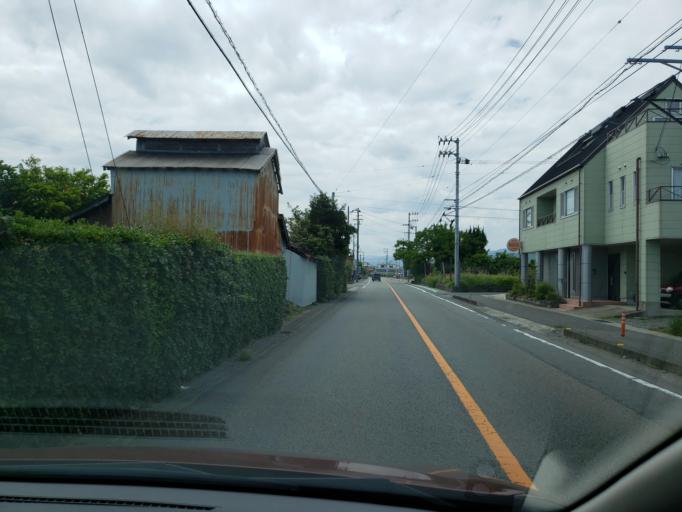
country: JP
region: Tokushima
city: Kamojimacho-jogejima
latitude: 34.0965
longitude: 134.3501
